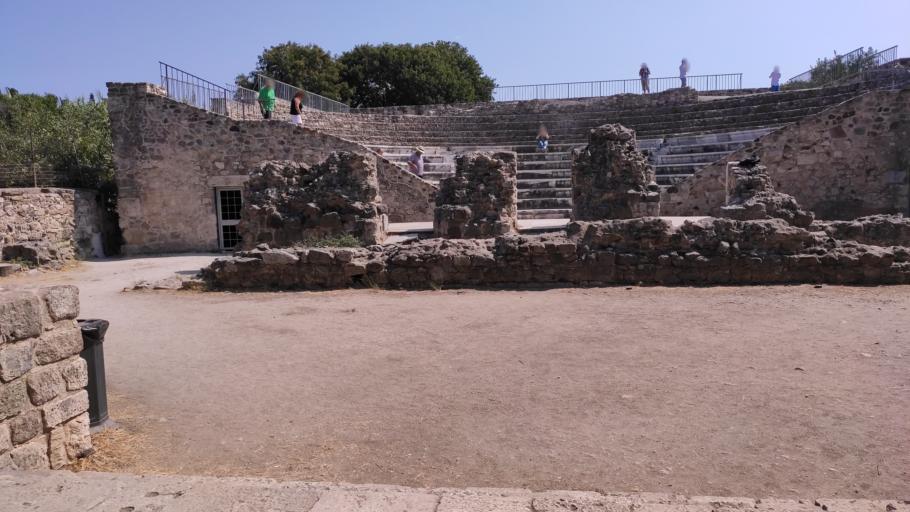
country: GR
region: South Aegean
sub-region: Nomos Dodekanisou
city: Kos
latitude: 36.8898
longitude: 27.2848
